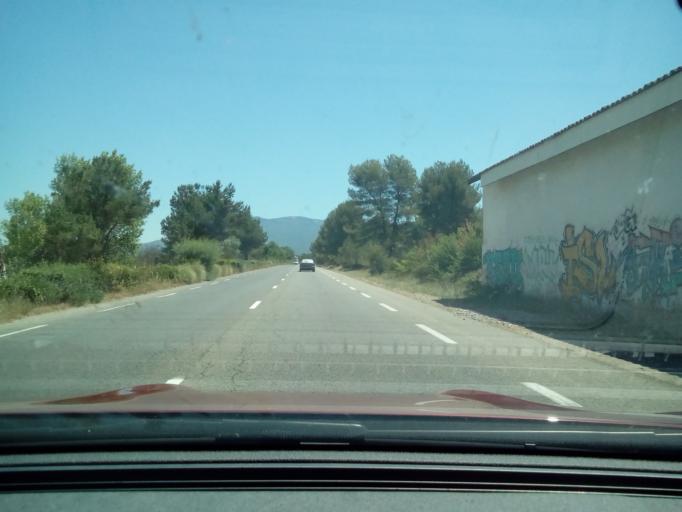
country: FR
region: Provence-Alpes-Cote d'Azur
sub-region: Departement des Bouches-du-Rhone
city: Peynier
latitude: 43.4596
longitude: 5.6462
